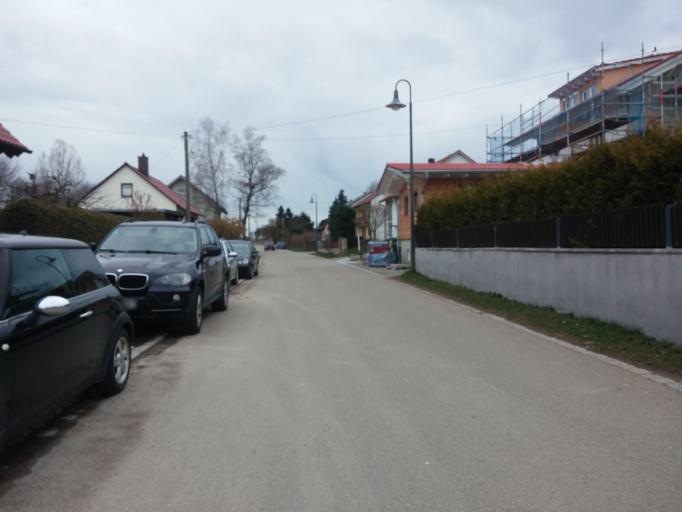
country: DE
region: Bavaria
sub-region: Swabia
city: Holzgunz
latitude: 48.0146
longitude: 10.2427
